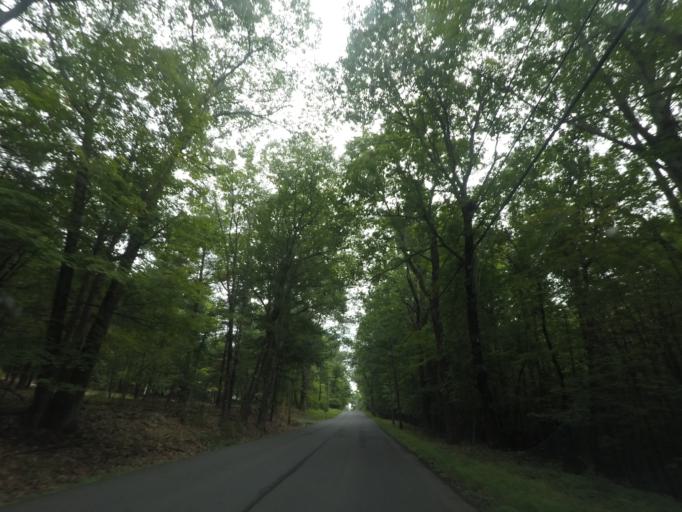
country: US
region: New York
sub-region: Rensselaer County
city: Nassau
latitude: 42.5001
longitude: -73.6050
